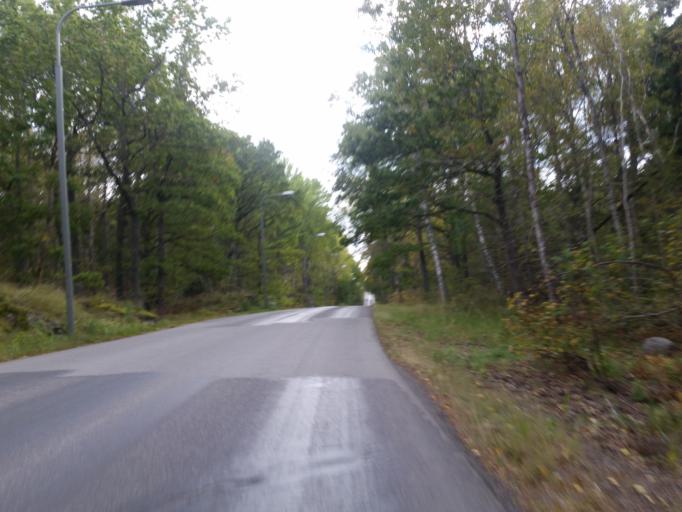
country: SE
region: Stockholm
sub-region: Nacka Kommun
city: Alta
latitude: 59.2546
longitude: 18.1360
